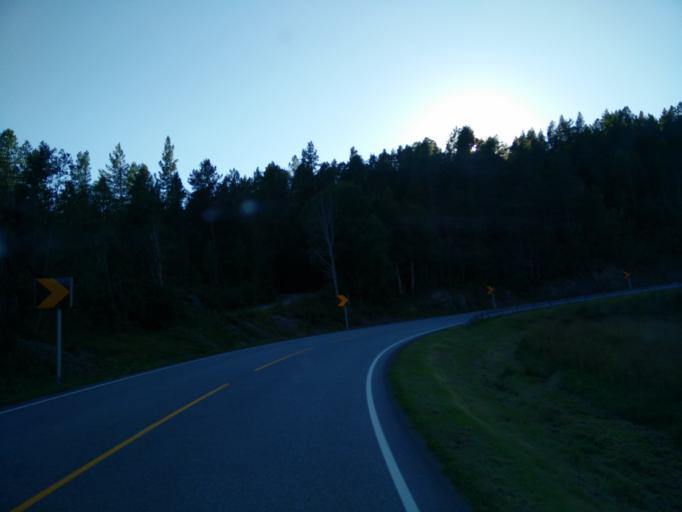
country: NO
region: More og Romsdal
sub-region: Halsa
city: Liaboen
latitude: 63.0245
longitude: 8.4623
